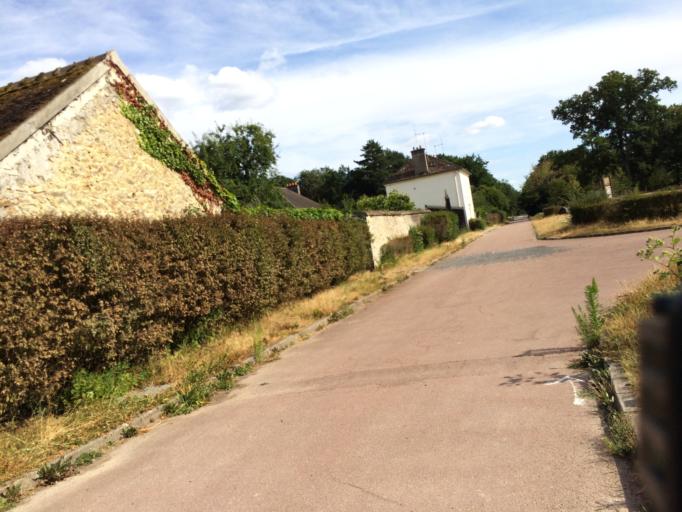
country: FR
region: Ile-de-France
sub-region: Departement de l'Essonne
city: Tigery
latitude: 48.6569
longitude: 2.4921
